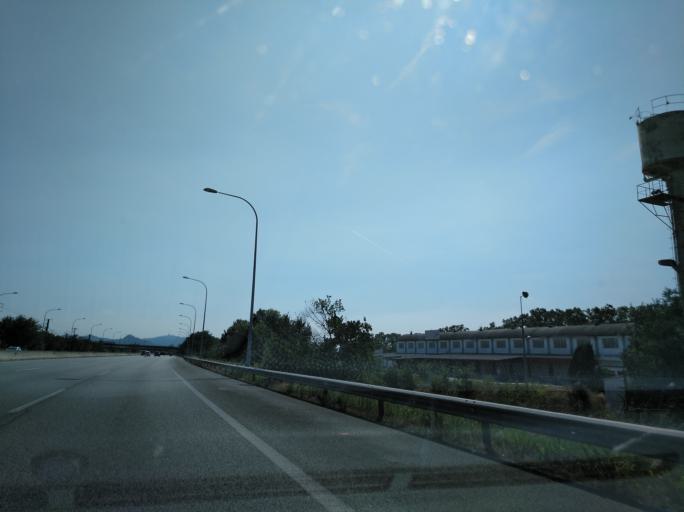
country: ES
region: Catalonia
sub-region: Provincia de Barcelona
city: Mollet del Valles
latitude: 41.5357
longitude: 2.2234
